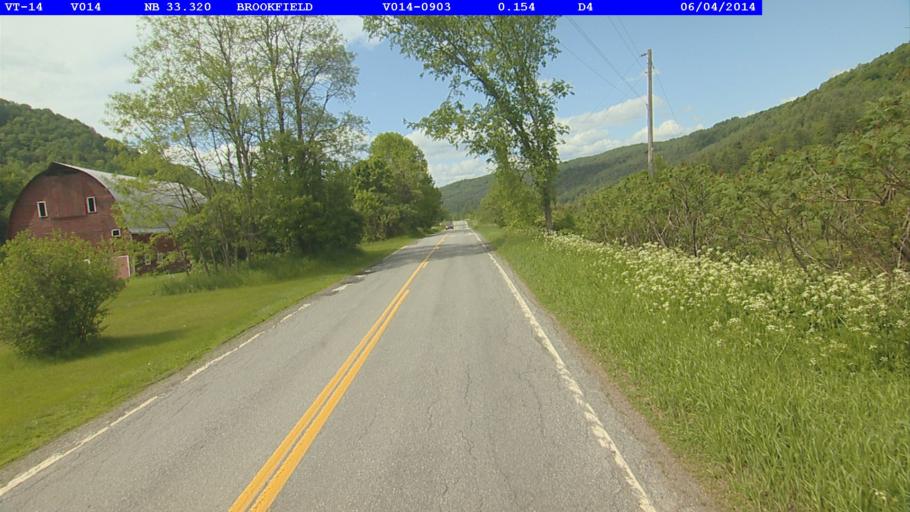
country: US
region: Vermont
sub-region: Orange County
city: Chelsea
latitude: 43.9813
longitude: -72.5573
